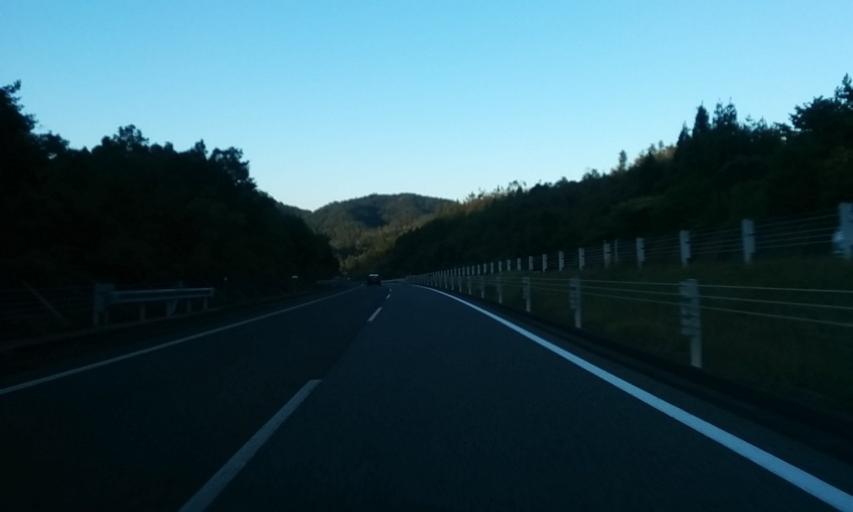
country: JP
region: Kyoto
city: Ayabe
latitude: 35.2247
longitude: 135.1851
